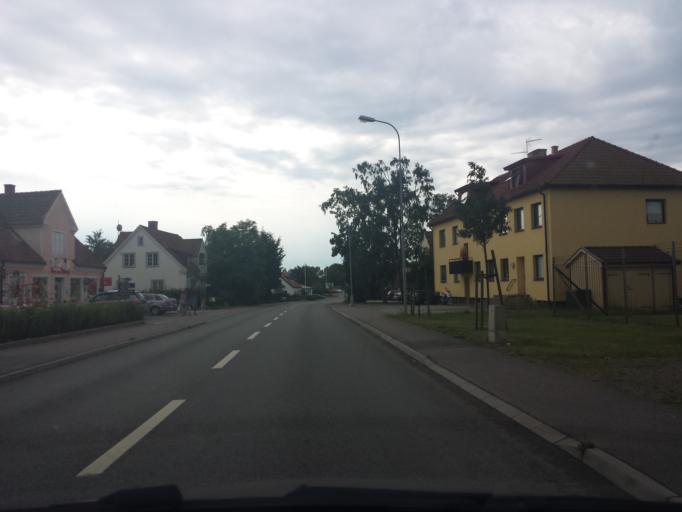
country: SE
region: Skane
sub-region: Ystads Kommun
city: Kopingebro
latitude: 55.4524
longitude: 14.0204
